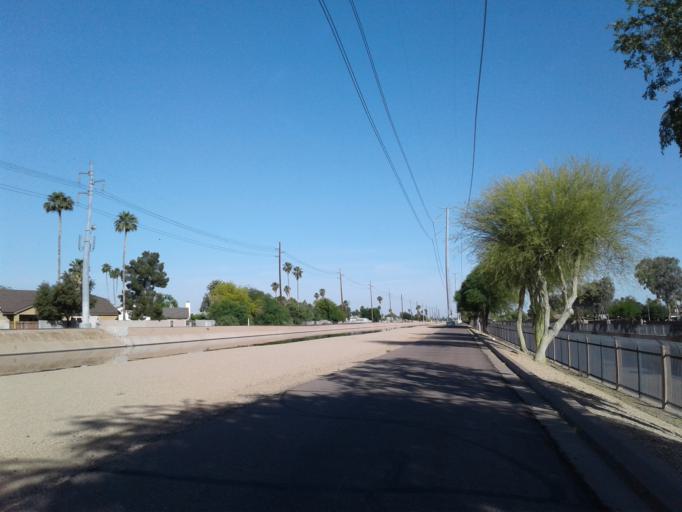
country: US
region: Arizona
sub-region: Maricopa County
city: Glendale
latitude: 33.5763
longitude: -112.1422
